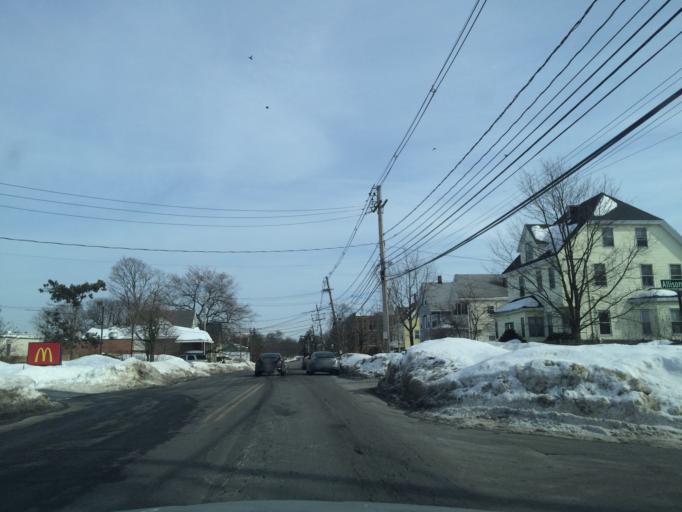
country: US
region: Massachusetts
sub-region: Middlesex County
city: Watertown
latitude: 42.3647
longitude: -71.1968
